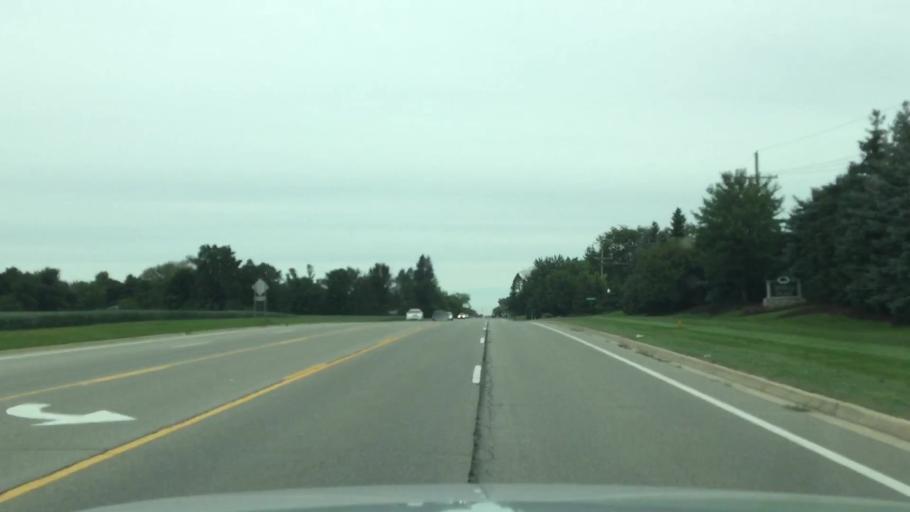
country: US
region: Michigan
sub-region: Washtenaw County
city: Ypsilanti
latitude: 42.2027
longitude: -83.6794
